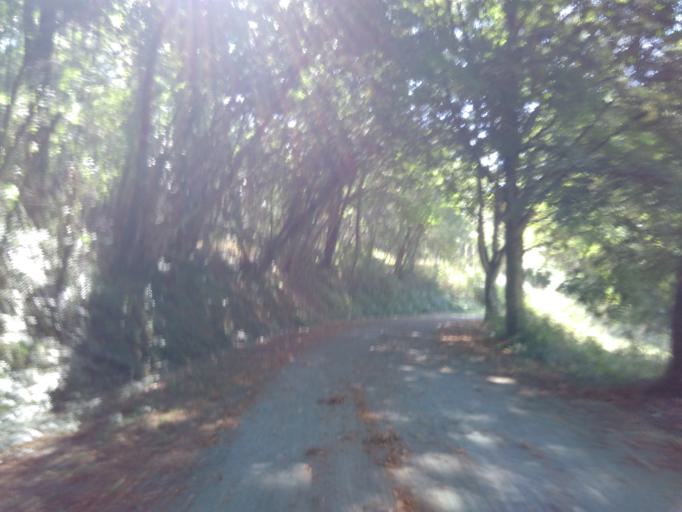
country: FR
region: Pays de la Loire
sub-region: Departement de la Vendee
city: La Chaize-le-Vicomte
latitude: 46.6620
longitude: -1.3030
